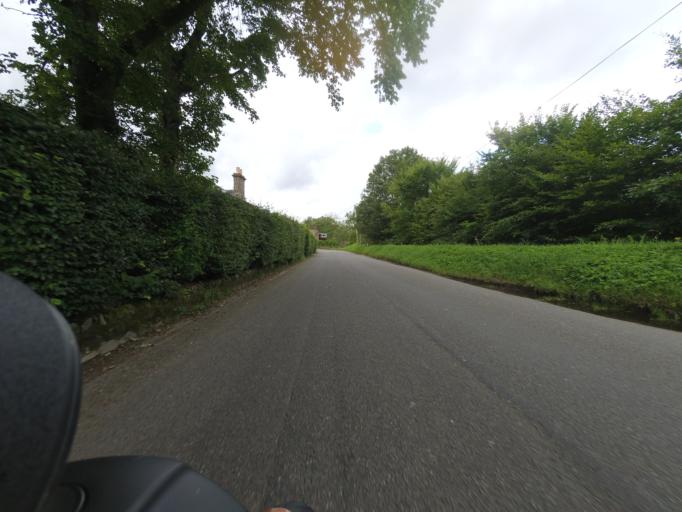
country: GB
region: Scotland
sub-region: Aberdeenshire
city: Laurencekirk
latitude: 56.8472
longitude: -2.5687
